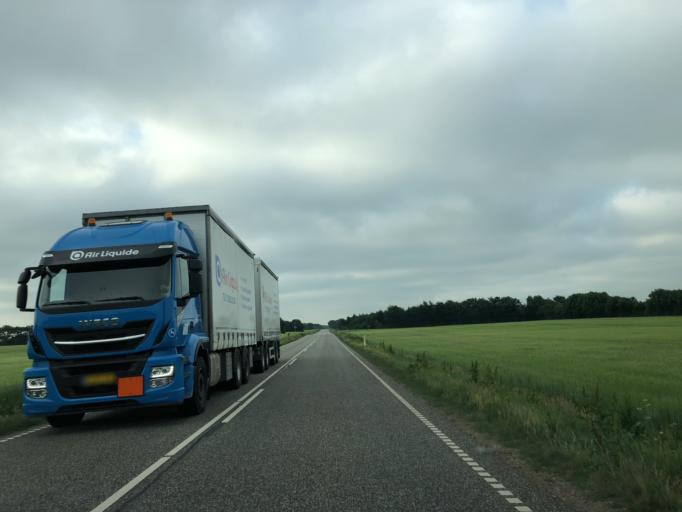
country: DK
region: South Denmark
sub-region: Vejle Kommune
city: Give
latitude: 55.9006
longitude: 9.2019
